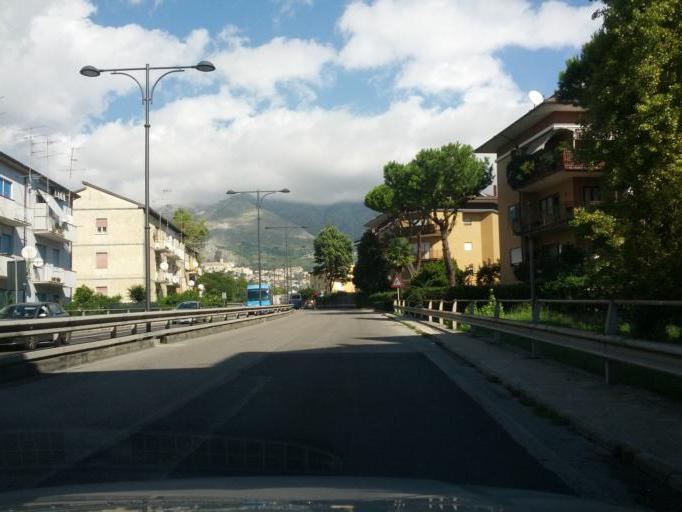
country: IT
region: Latium
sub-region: Provincia di Latina
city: Formia
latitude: 41.2623
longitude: 13.6202
